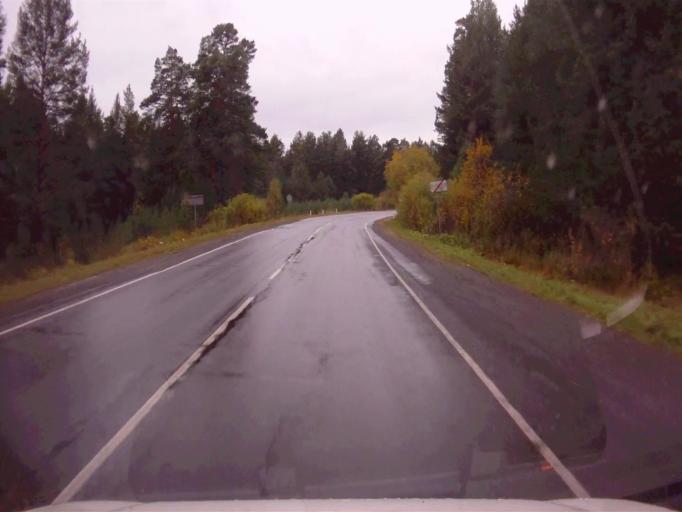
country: RU
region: Chelyabinsk
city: Verkhniy Ufaley
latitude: 56.0523
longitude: 60.1680
